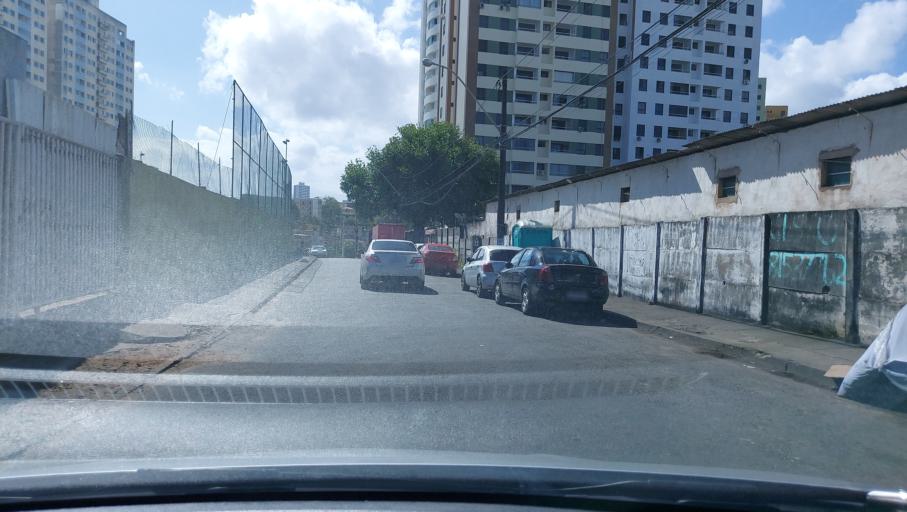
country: BR
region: Bahia
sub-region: Salvador
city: Salvador
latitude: -12.9635
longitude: -38.4371
